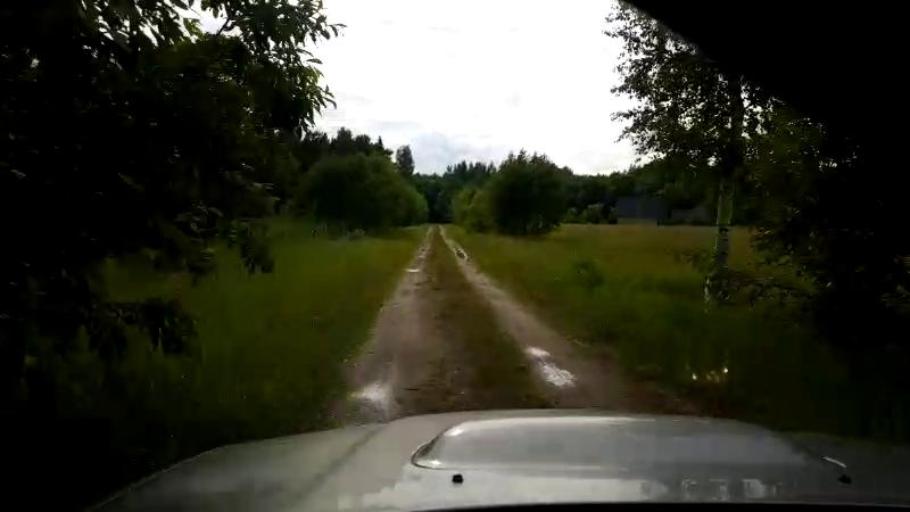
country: EE
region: Paernumaa
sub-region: Halinga vald
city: Parnu-Jaagupi
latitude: 58.5533
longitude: 24.5704
